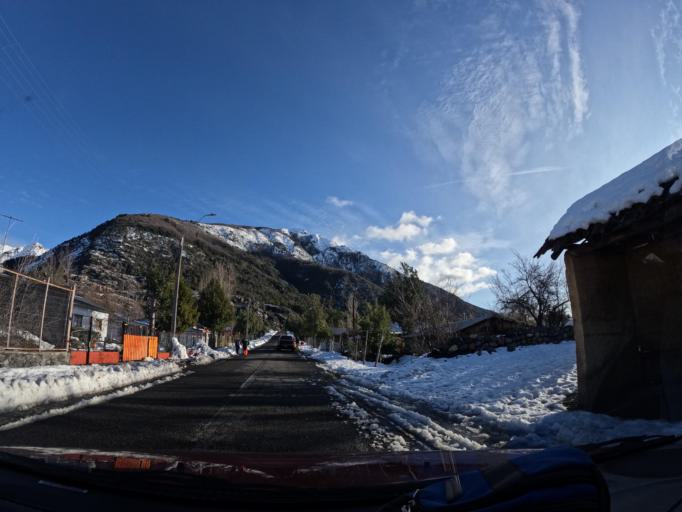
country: CL
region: Biobio
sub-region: Provincia de Nuble
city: Coihueco
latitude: -37.3696
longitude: -71.4912
